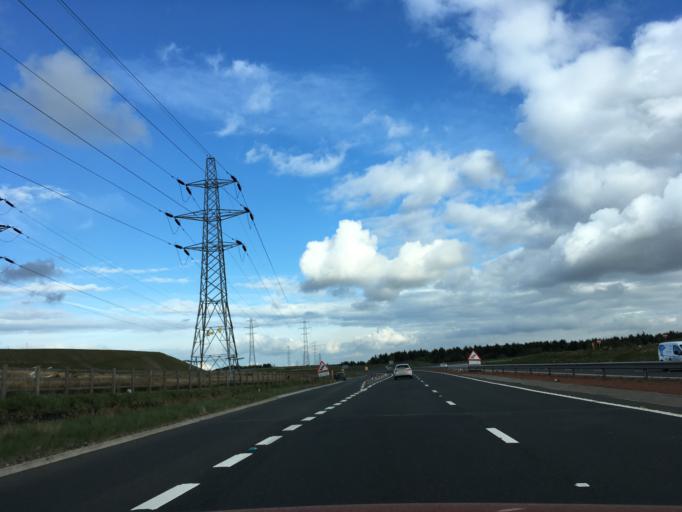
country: GB
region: Wales
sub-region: Blaenau Gwent
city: Brynmawr
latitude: 51.8076
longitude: -3.2039
